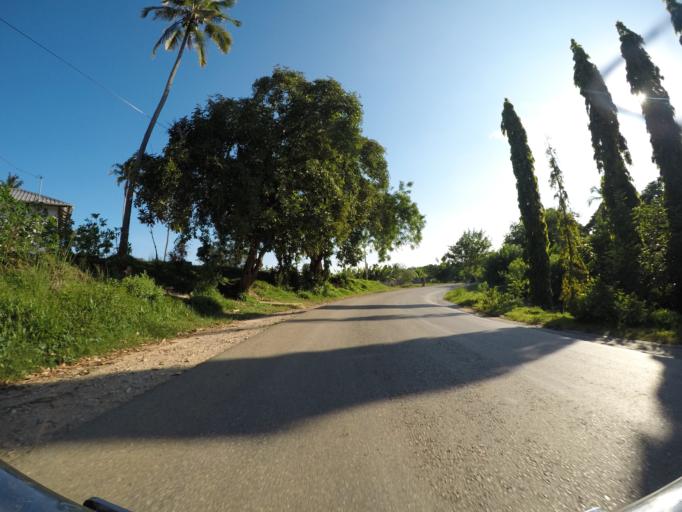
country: TZ
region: Pemba South
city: Chake Chake
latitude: -5.3068
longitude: 39.7495
